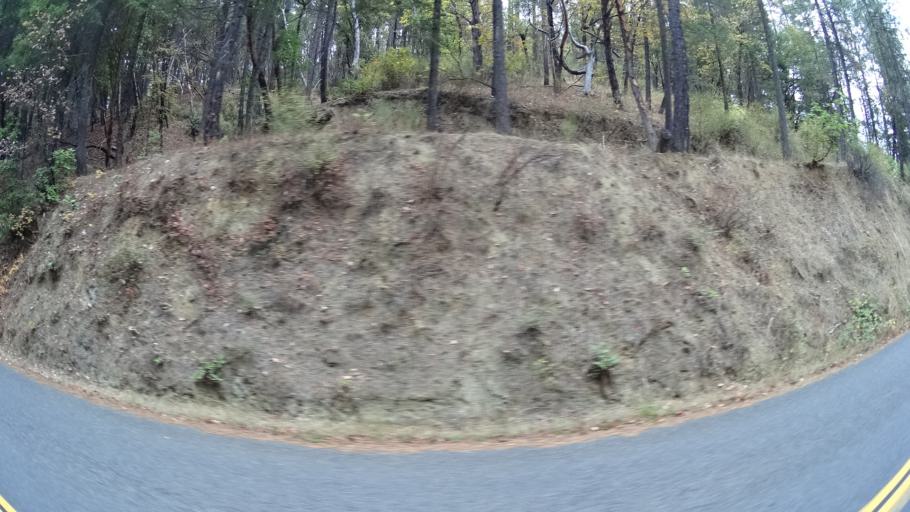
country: US
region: California
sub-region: Siskiyou County
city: Happy Camp
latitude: 41.7816
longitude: -123.3883
